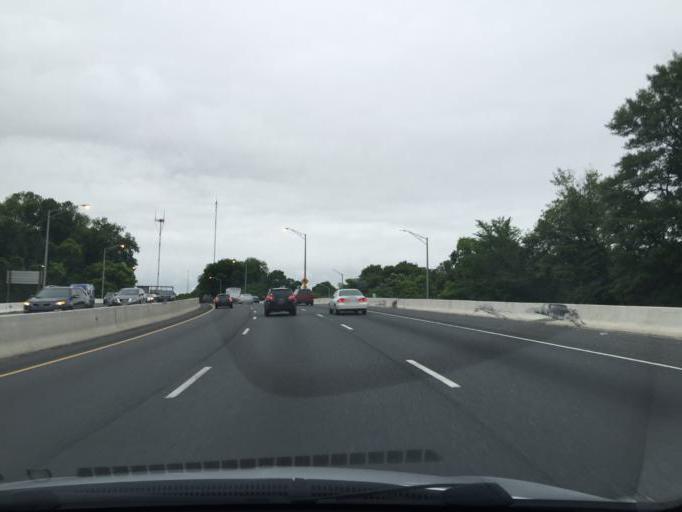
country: US
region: Maryland
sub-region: City of Baltimore
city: Baltimore
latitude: 39.3237
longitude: -76.6327
